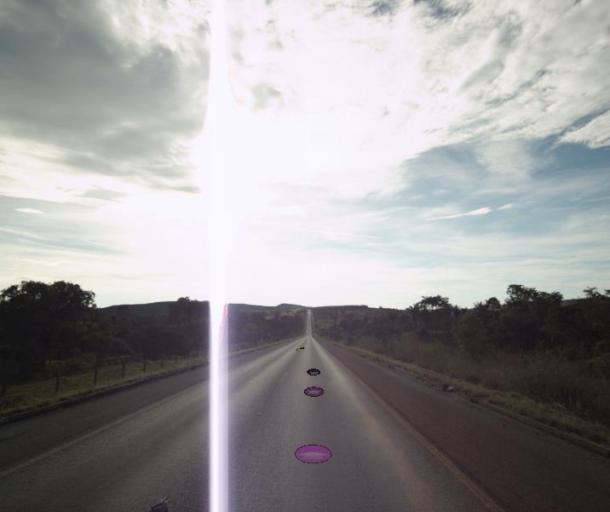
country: BR
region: Goias
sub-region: Pirenopolis
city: Pirenopolis
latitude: -15.7510
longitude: -48.6322
